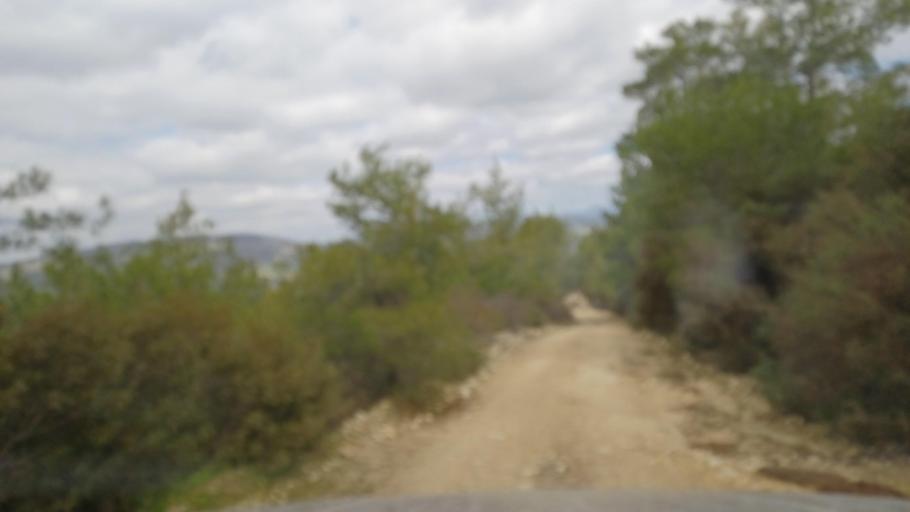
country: CY
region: Limassol
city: Pachna
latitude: 34.7720
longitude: 32.6948
